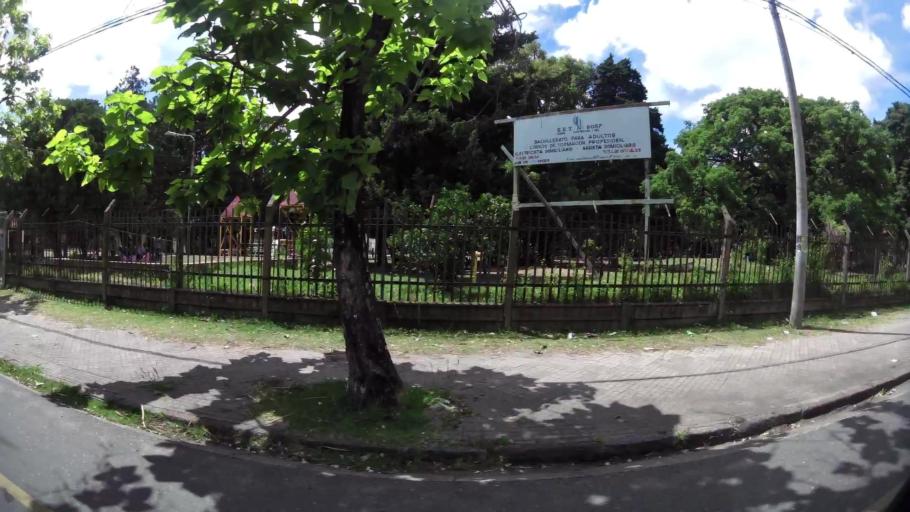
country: AR
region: Santa Fe
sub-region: Departamento de Rosario
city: Rosario
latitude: -32.9713
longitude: -60.6341
